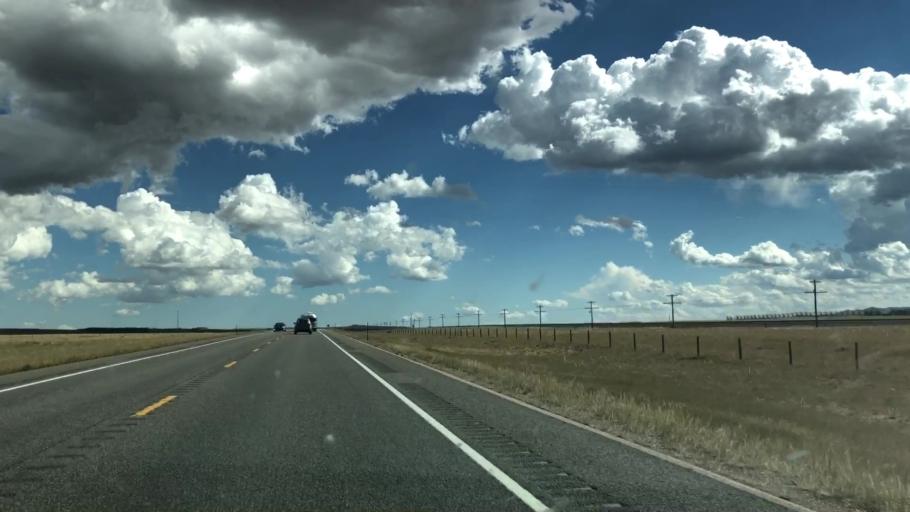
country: US
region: Wyoming
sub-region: Albany County
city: Laramie
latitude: 41.1525
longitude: -105.5709
